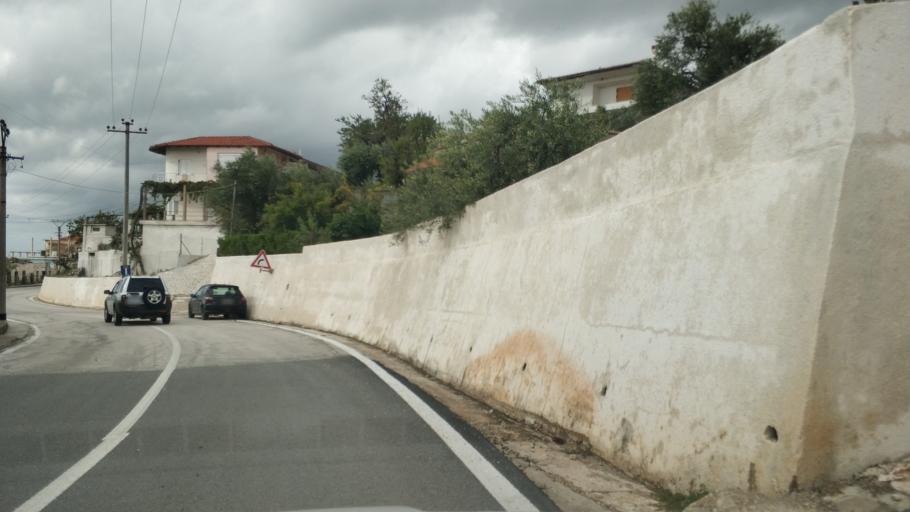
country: AL
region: Vlore
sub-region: Rrethi i Vlores
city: Vranisht
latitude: 40.1511
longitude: 19.6400
